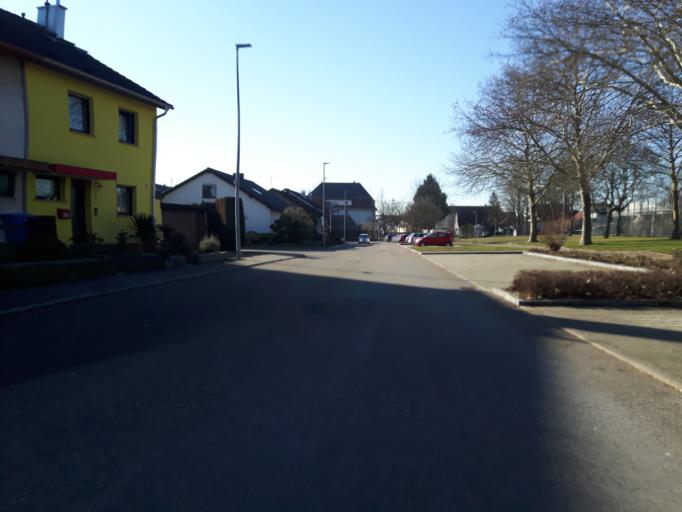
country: DE
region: Baden-Wuerttemberg
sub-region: Regierungsbezirk Stuttgart
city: Bonnigheim
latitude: 49.0667
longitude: 9.0909
